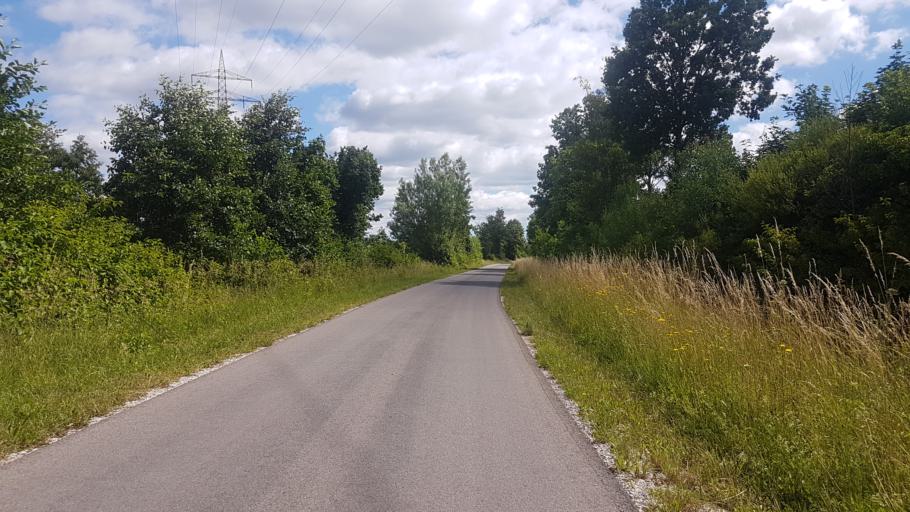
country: DE
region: Bavaria
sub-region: Regierungsbezirk Mittelfranken
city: Gunzenhausen
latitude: 49.1256
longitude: 10.7545
